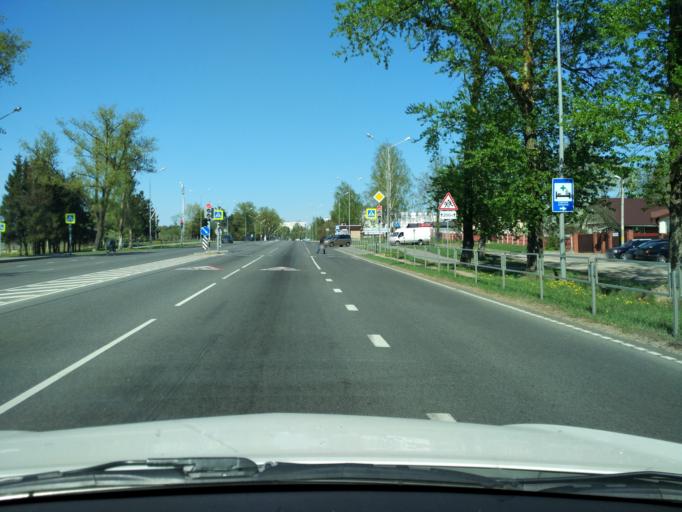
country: BY
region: Minsk
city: Borovlyany
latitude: 53.9953
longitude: 27.6730
